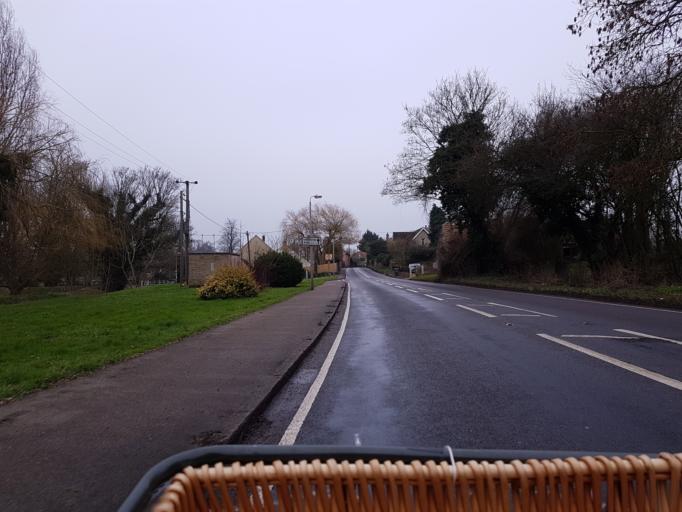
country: GB
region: England
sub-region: Cambridgeshire
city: Duxford
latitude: 52.0667
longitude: 0.1932
